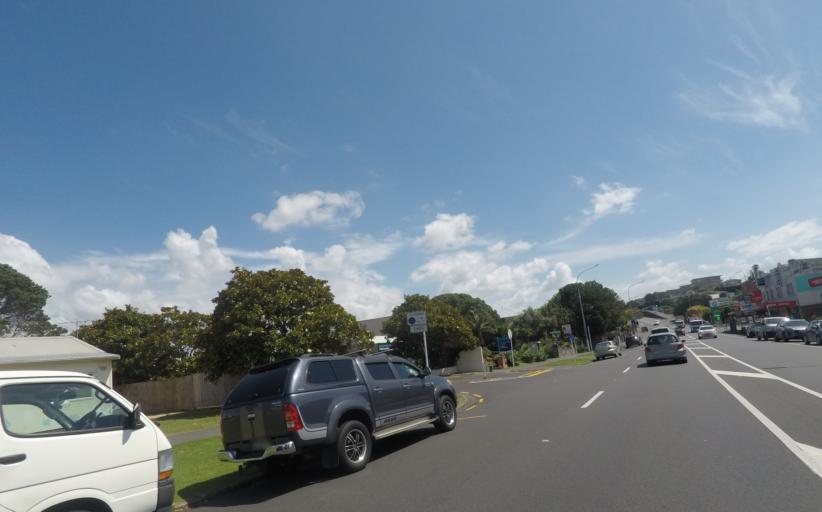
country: NZ
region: Auckland
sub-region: Auckland
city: Tamaki
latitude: -36.8761
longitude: 174.8269
